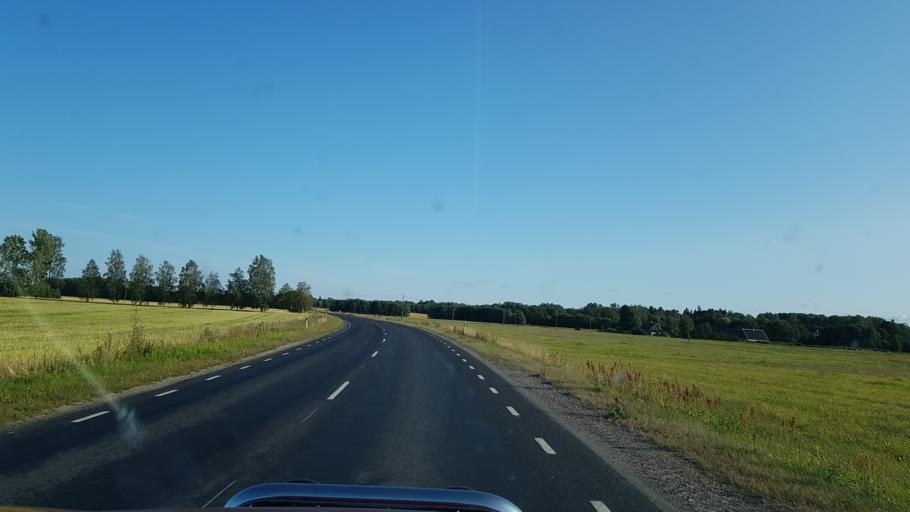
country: EE
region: Harju
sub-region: Raasiku vald
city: Raasiku
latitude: 59.1381
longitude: 25.2015
